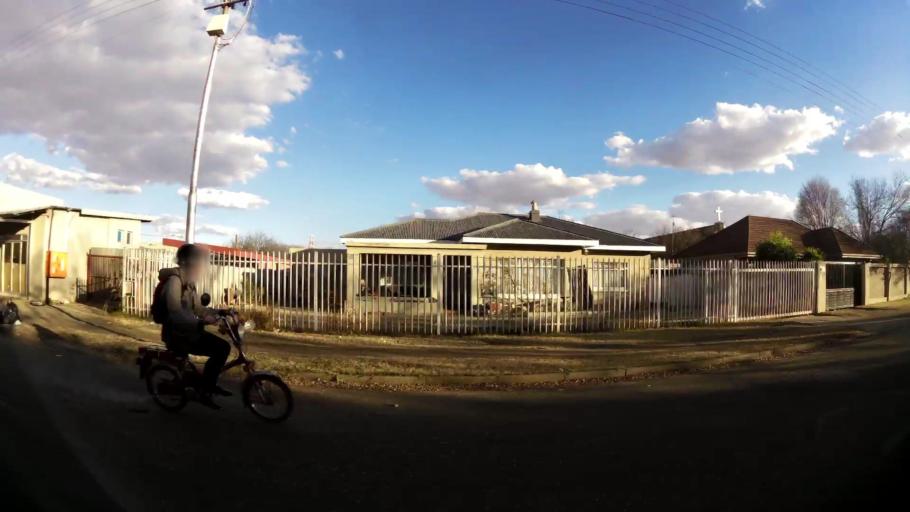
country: ZA
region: North-West
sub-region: Dr Kenneth Kaunda District Municipality
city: Potchefstroom
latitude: -26.7244
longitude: 27.0958
